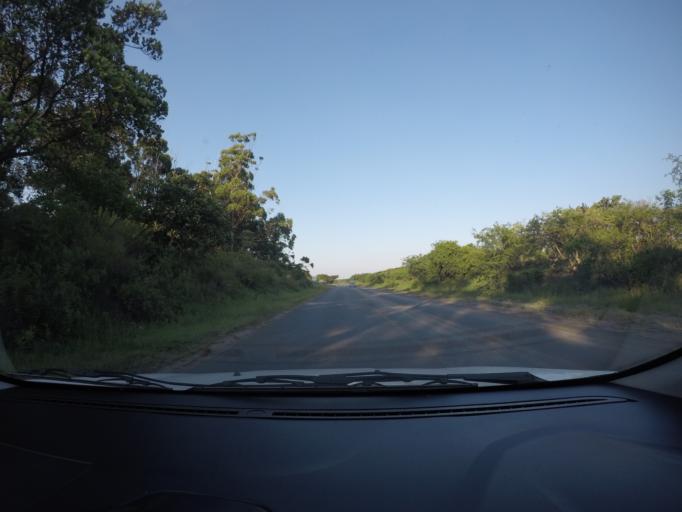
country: ZA
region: KwaZulu-Natal
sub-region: uThungulu District Municipality
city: Richards Bay
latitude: -28.7557
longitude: 32.0056
